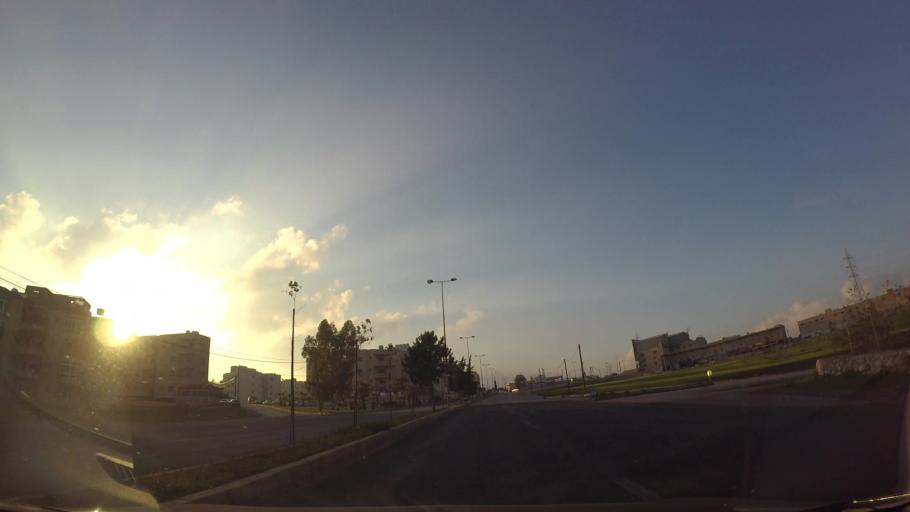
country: JO
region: Amman
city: Amman
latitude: 31.9857
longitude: 35.9523
